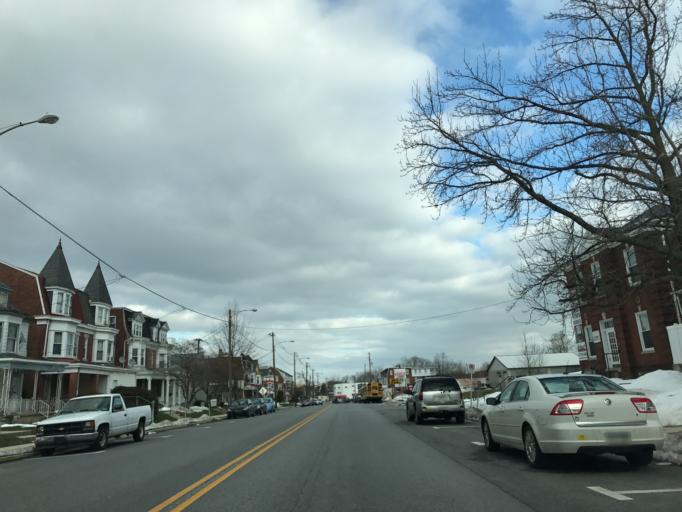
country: US
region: Pennsylvania
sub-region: York County
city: West York
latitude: 39.9537
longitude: -76.7582
